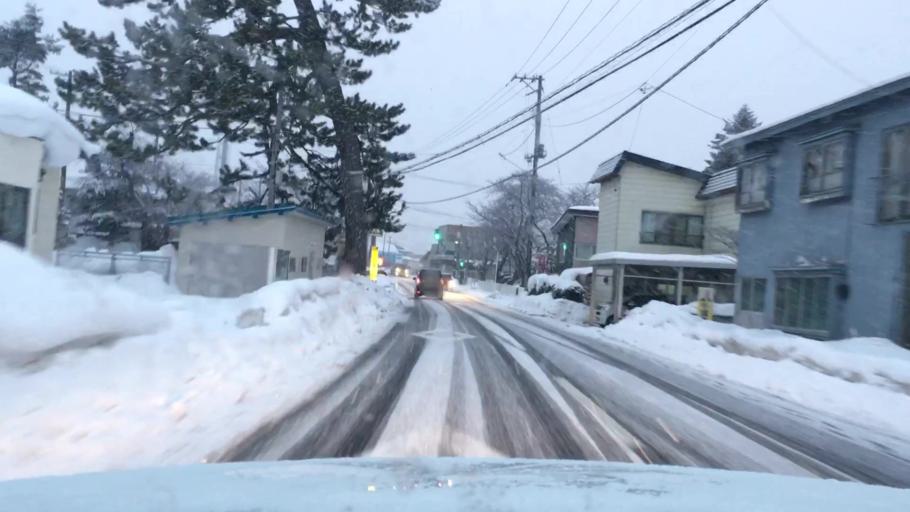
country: JP
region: Aomori
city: Hirosaki
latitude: 40.5654
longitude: 140.4853
